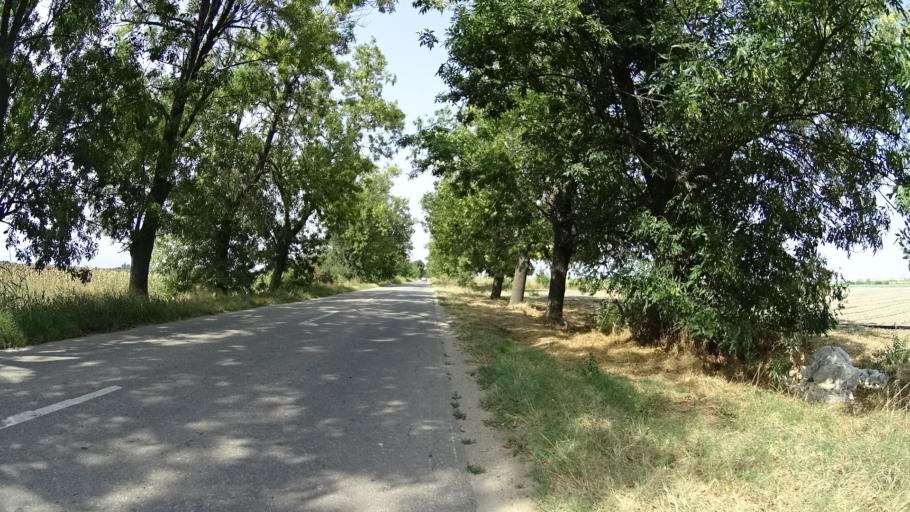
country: BG
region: Plovdiv
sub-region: Obshtina Plovdiv
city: Plovdiv
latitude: 42.2515
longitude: 24.7977
